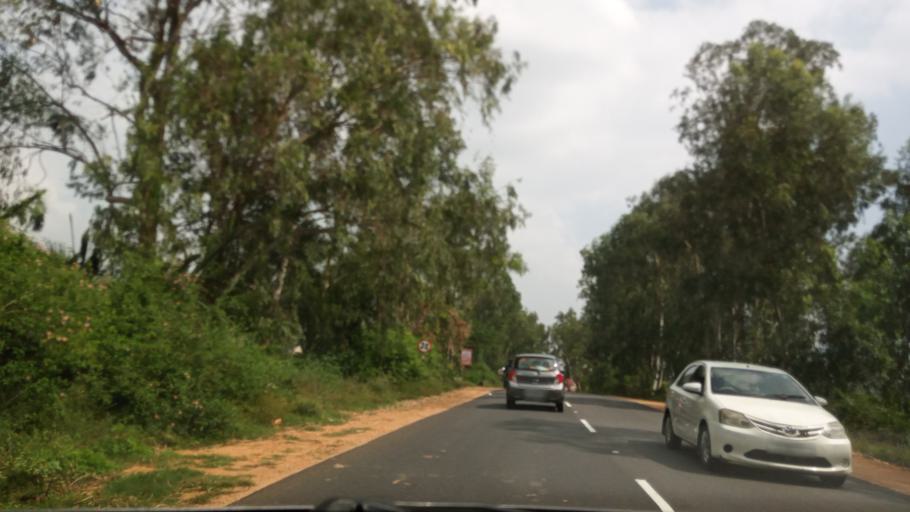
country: IN
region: Andhra Pradesh
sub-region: Chittoor
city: Madanapalle
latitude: 13.6357
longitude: 78.6041
